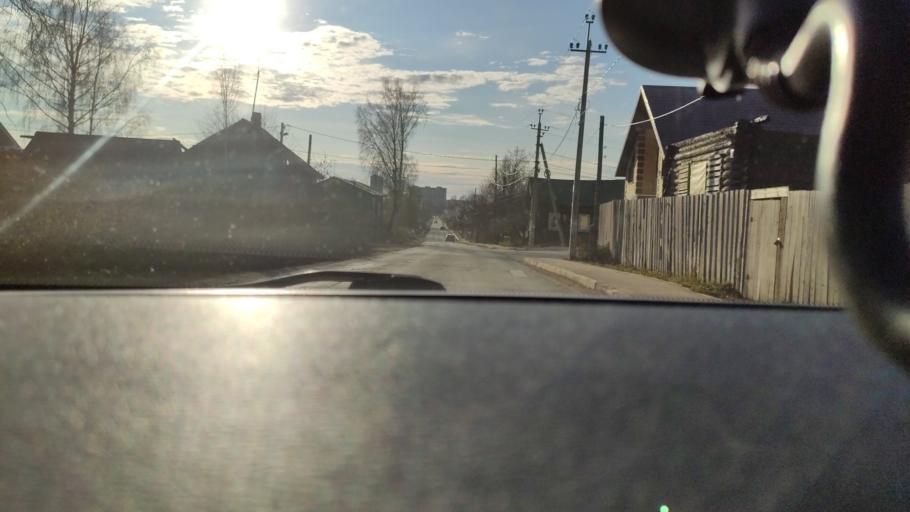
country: RU
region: Perm
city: Kondratovo
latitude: 58.0525
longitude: 56.0287
